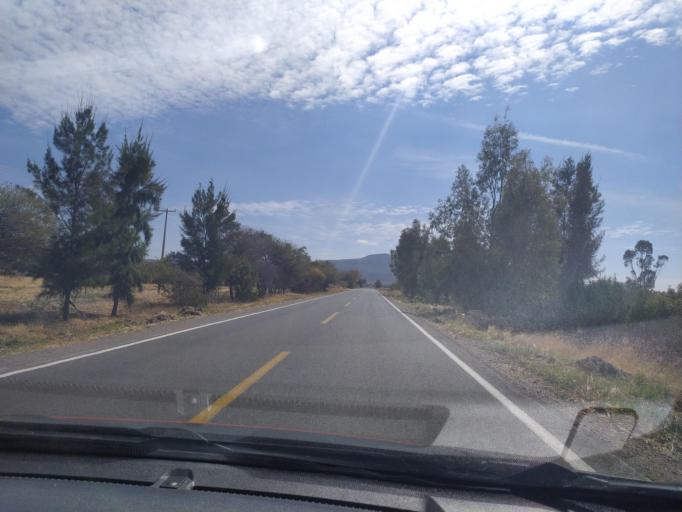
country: MX
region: Guanajuato
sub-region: San Francisco del Rincon
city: San Ignacio de Hidalgo
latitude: 20.8528
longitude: -101.8552
